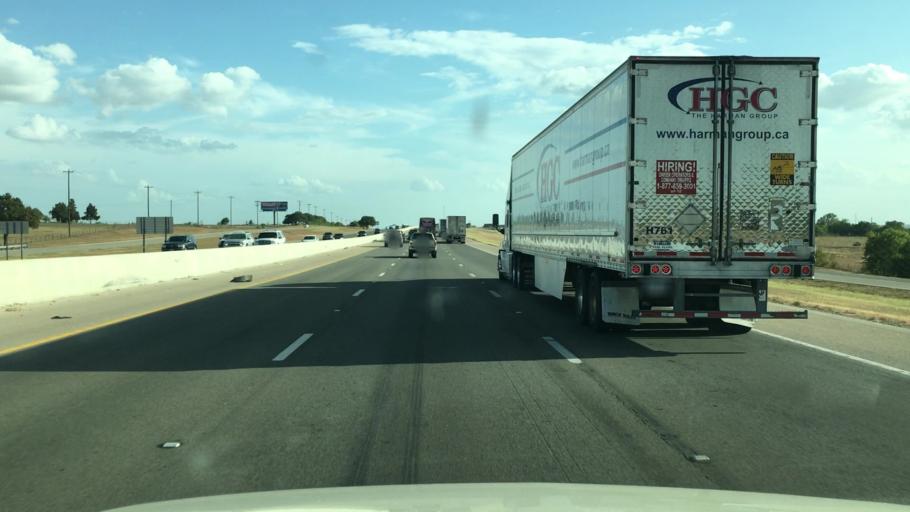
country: US
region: Texas
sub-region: Williamson County
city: Serenada
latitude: 30.7626
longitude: -97.6306
